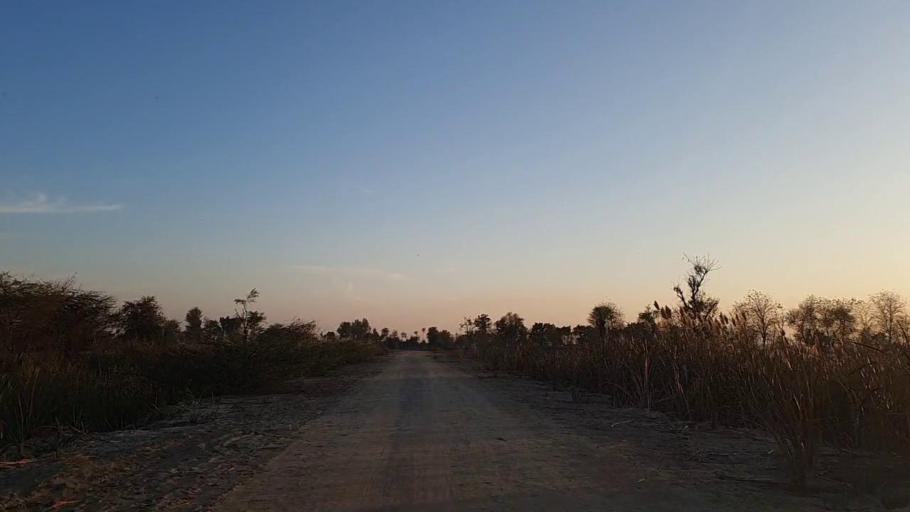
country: PK
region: Sindh
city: Bandhi
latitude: 26.6290
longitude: 68.3706
